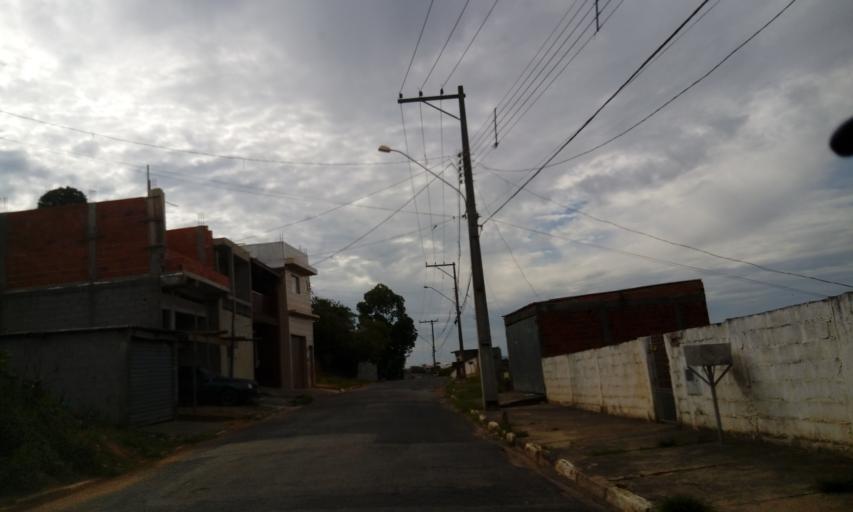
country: BR
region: Sao Paulo
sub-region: Francisco Morato
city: Francisco Morato
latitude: -23.2651
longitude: -46.7462
